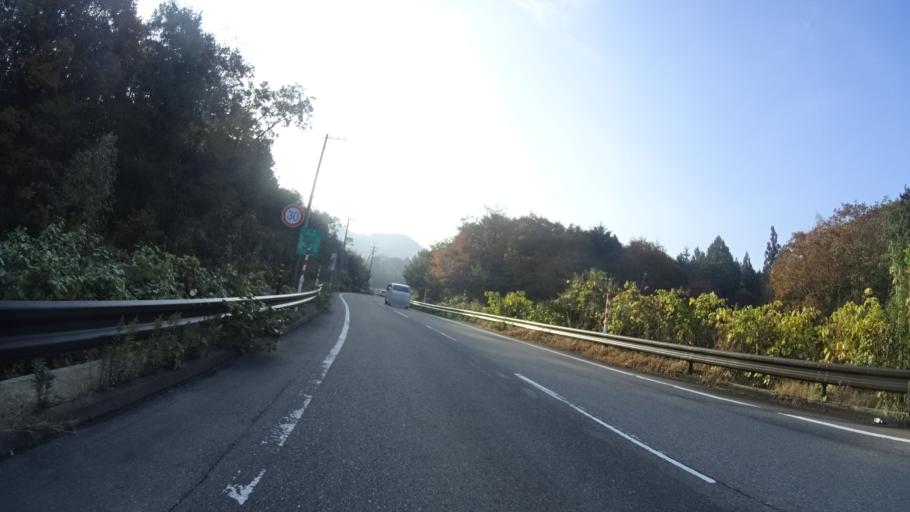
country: JP
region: Ishikawa
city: Nanao
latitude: 37.0239
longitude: 136.9851
